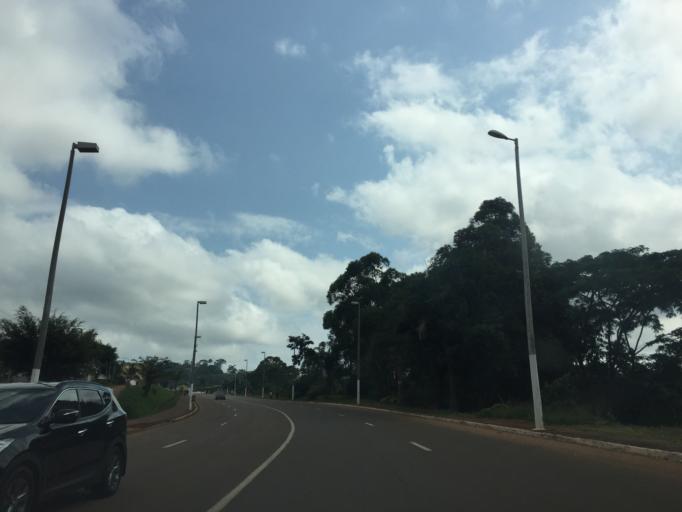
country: CM
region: Centre
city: Yaounde
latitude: 3.9020
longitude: 11.5046
